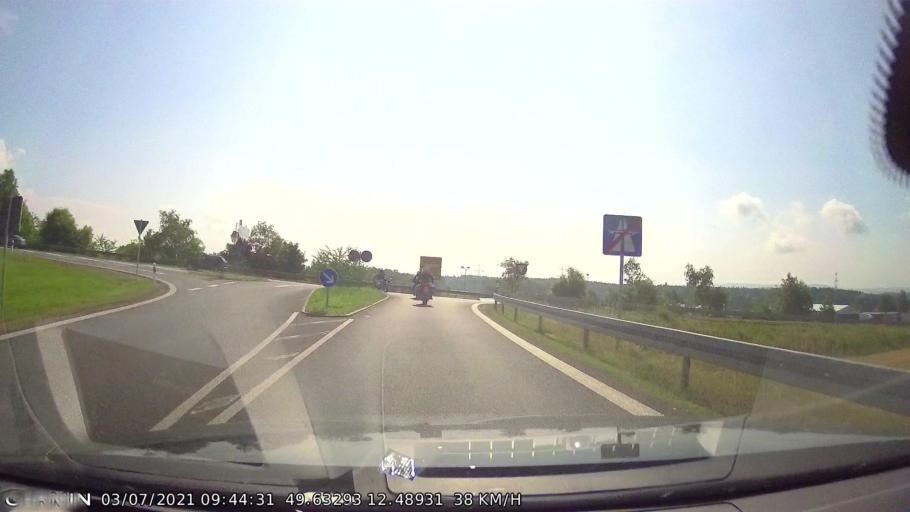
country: DE
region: Bavaria
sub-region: Upper Palatinate
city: Waidhaus
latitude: 49.6330
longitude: 12.4891
